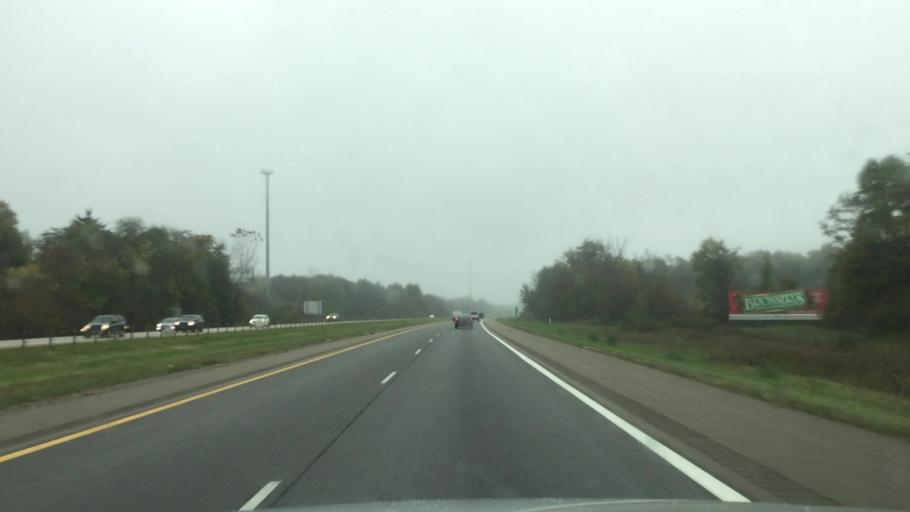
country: US
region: Michigan
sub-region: Van Buren County
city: Hartford
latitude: 42.1878
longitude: -86.2027
